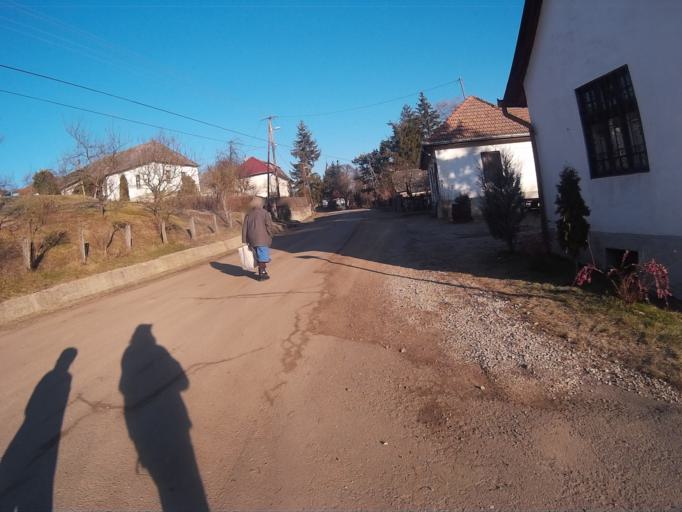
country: HU
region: Borsod-Abauj-Zemplen
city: Putnok
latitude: 48.3734
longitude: 20.4271
